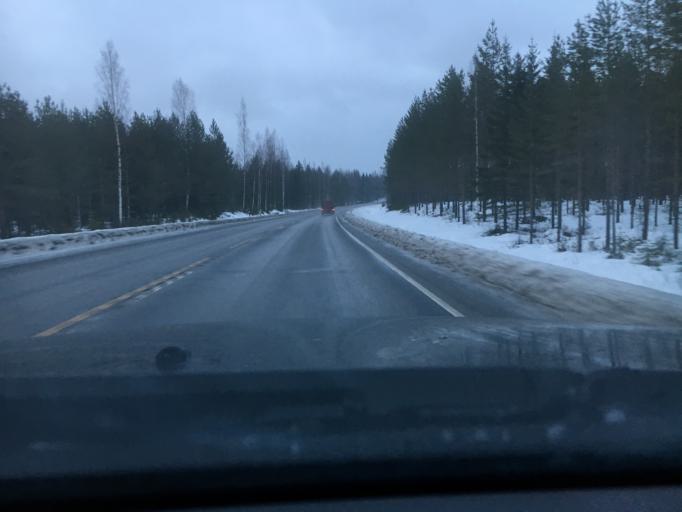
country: FI
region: Central Finland
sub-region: Jyvaeskylae
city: Hankasalmi
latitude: 62.4007
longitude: 26.6496
